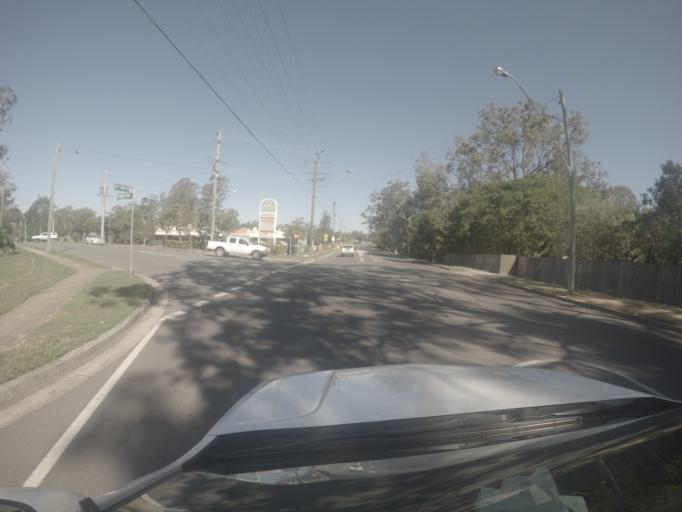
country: AU
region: Queensland
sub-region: Ipswich
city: Springfield
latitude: -27.6354
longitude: 152.9163
